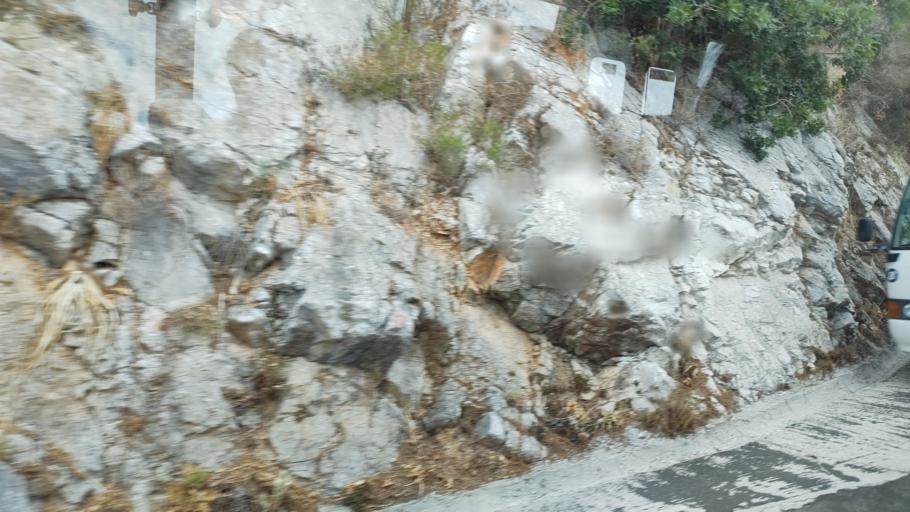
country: GI
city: Gibraltar
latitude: 36.1279
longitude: -5.3465
